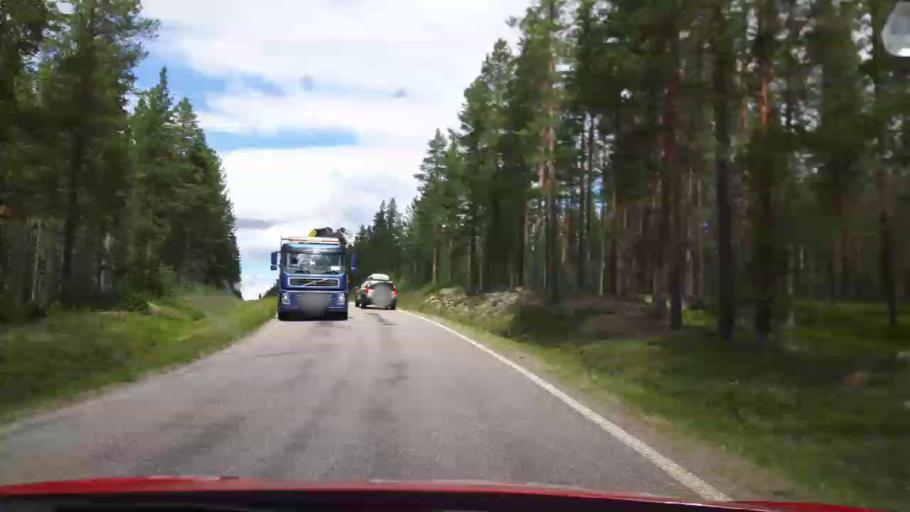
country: NO
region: Hedmark
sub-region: Trysil
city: Innbygda
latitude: 61.8364
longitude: 12.9571
